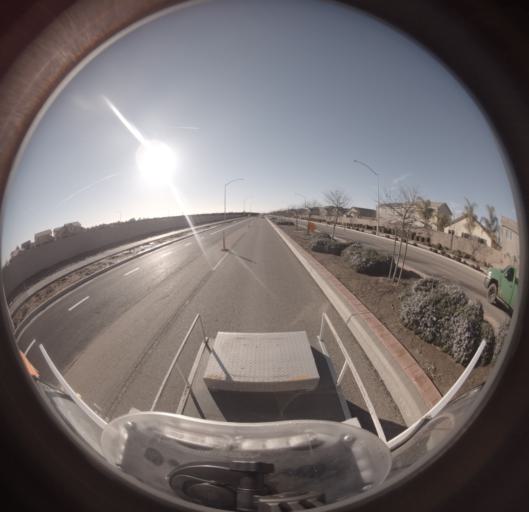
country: US
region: California
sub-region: Monterey County
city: King City
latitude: 36.1194
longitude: -120.8959
